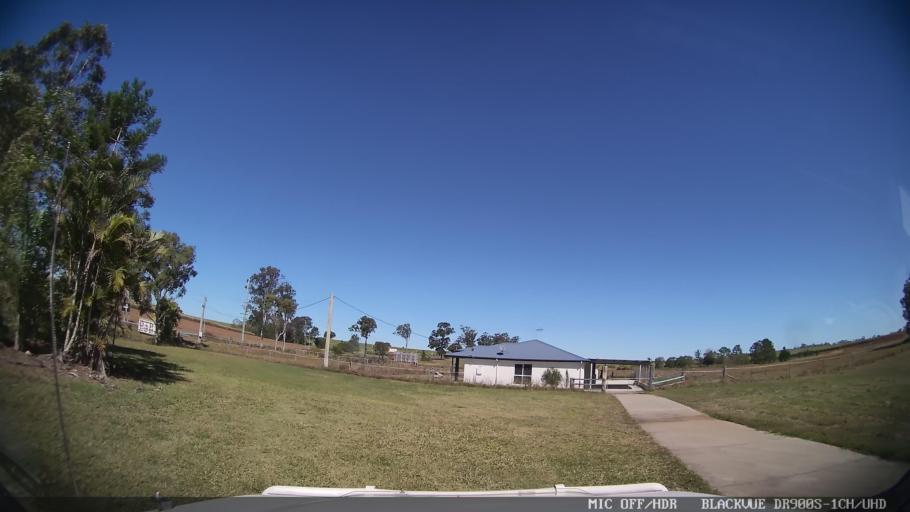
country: AU
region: Queensland
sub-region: Fraser Coast
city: Maryborough
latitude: -25.5777
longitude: 152.6540
